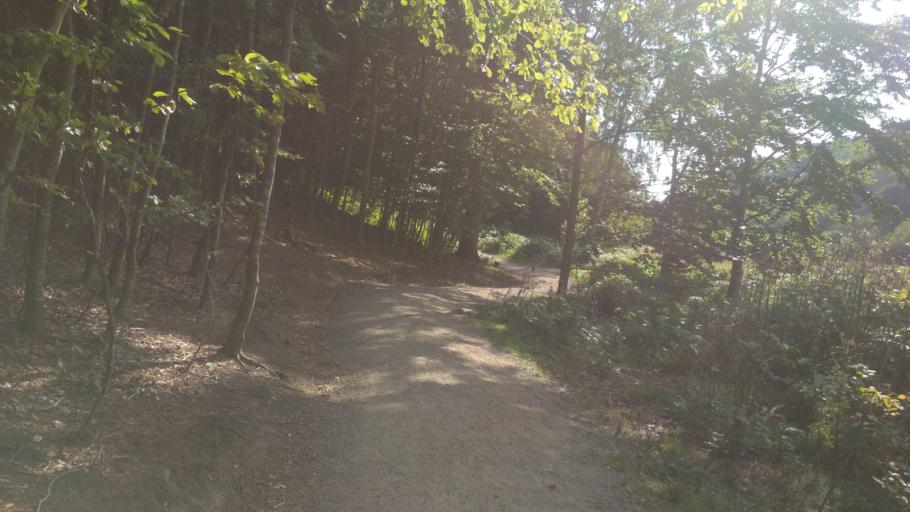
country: DK
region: Capital Region
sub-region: Bornholm Kommune
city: Akirkeby
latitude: 55.1061
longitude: 14.8970
